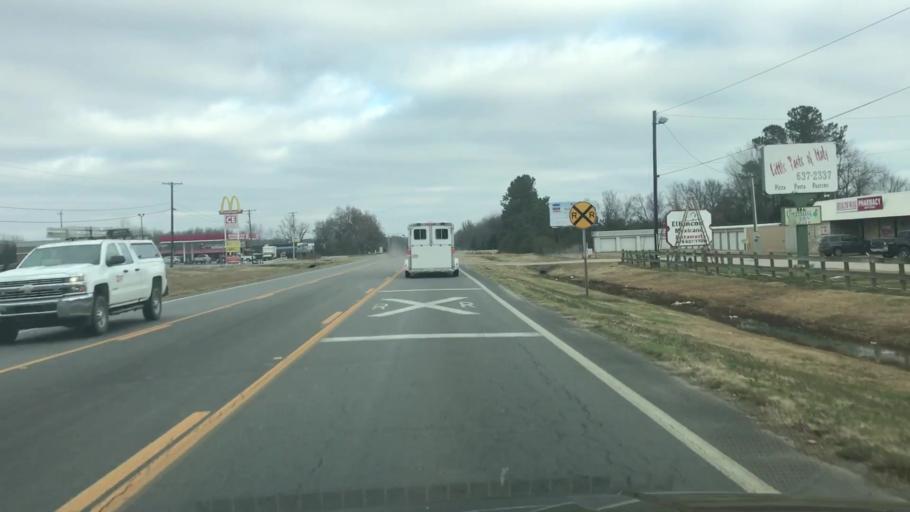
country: US
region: Arkansas
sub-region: Scott County
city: Waldron
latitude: 34.9027
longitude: -94.1074
